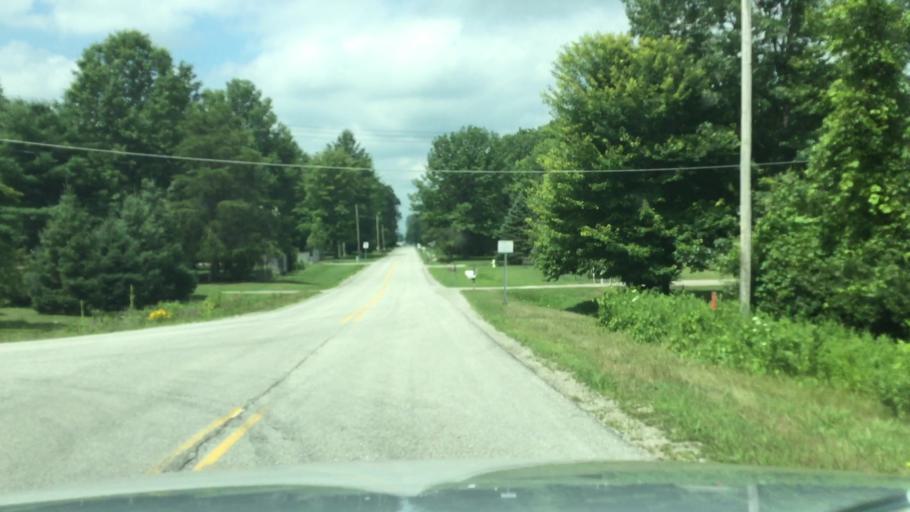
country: US
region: Michigan
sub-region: Saginaw County
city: Bridgeport
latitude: 43.3074
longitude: -83.8379
